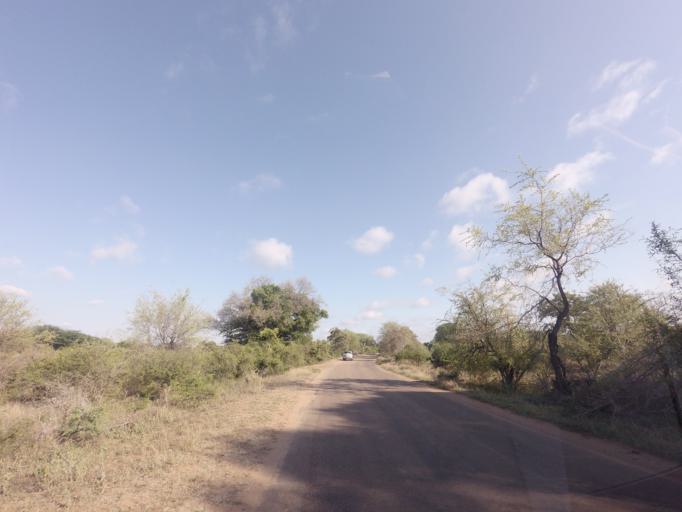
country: ZA
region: Mpumalanga
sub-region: Ehlanzeni District
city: Komatipoort
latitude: -25.2636
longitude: 31.8463
